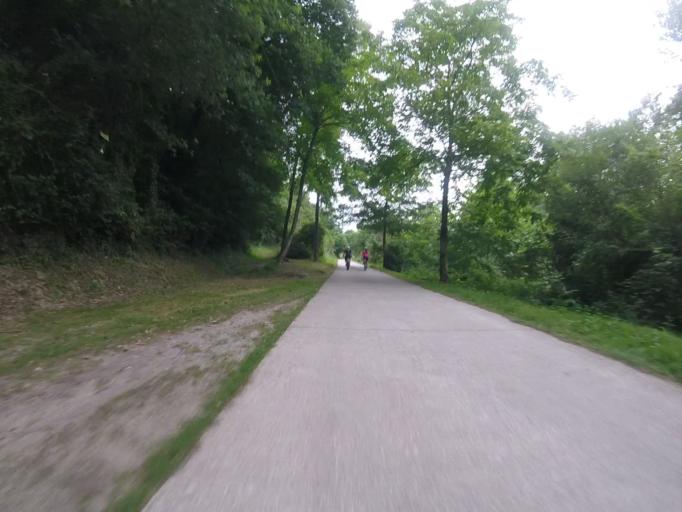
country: ES
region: Navarre
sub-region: Provincia de Navarra
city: Sunbilla
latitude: 43.1566
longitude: -1.6715
